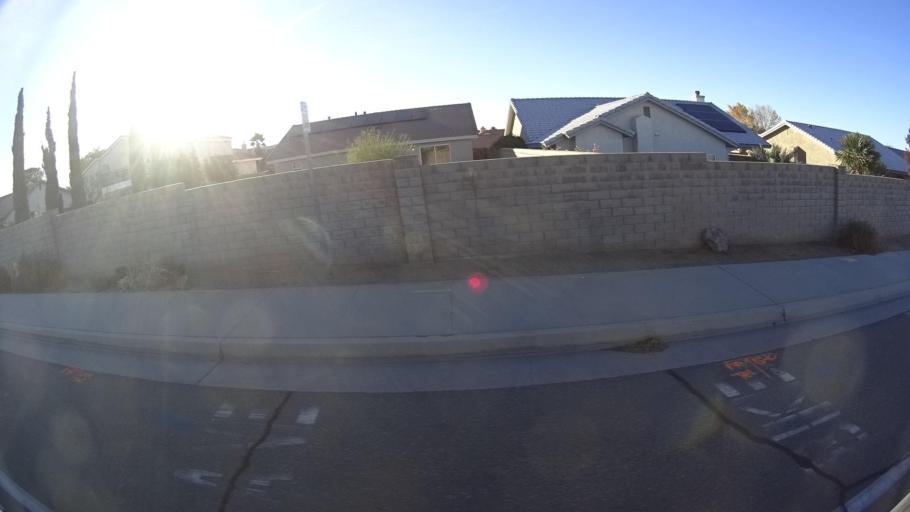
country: US
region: California
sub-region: Kern County
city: Ridgecrest
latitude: 35.5817
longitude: -117.6702
